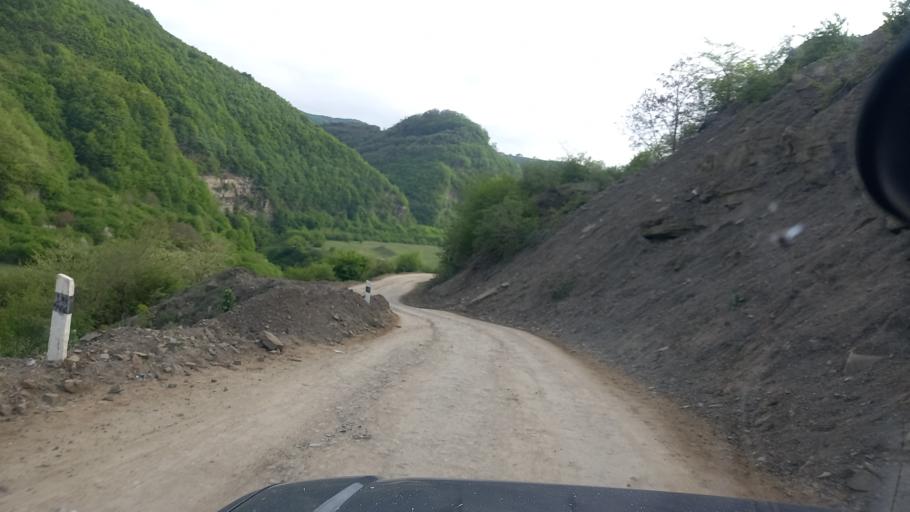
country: RU
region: Dagestan
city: Khuchni
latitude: 41.9662
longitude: 47.8737
